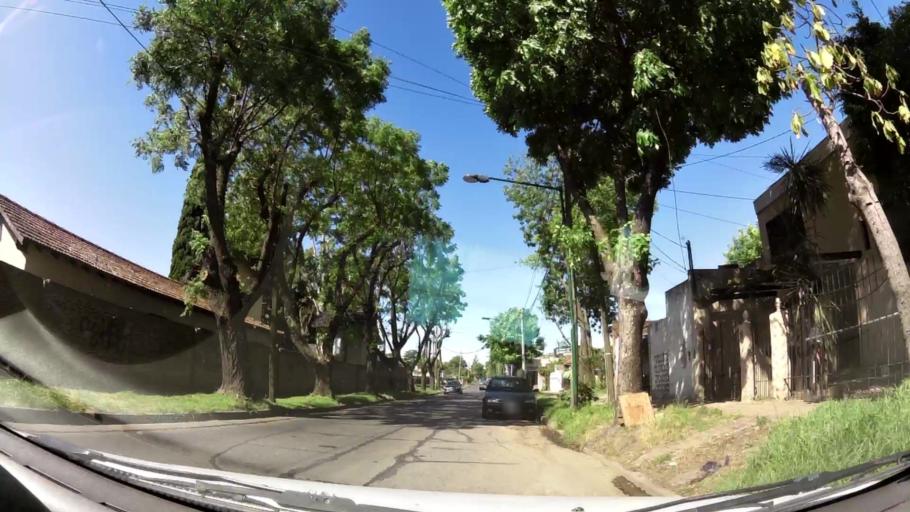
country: AR
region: Buenos Aires
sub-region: Partido de San Isidro
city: San Isidro
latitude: -34.4731
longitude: -58.5309
